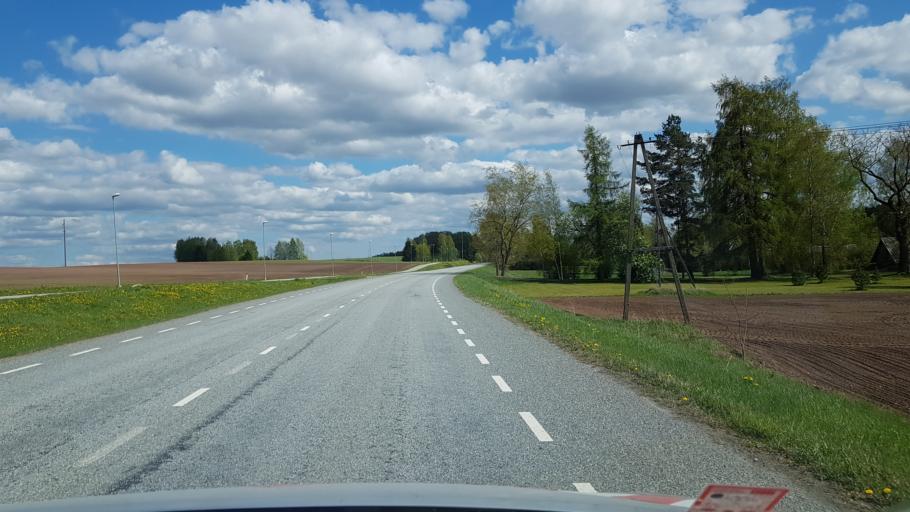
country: EE
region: Tartu
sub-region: UElenurme vald
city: Ulenurme
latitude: 58.2968
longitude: 26.8807
